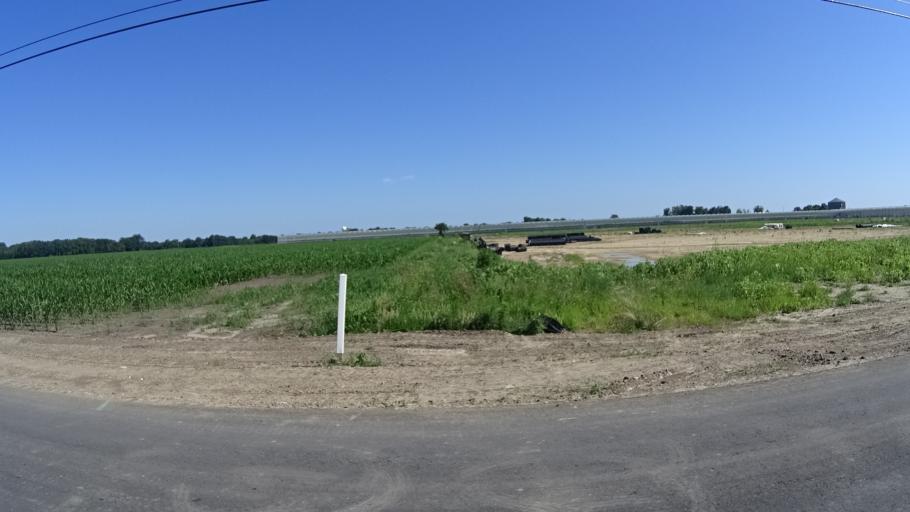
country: US
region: Ohio
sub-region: Erie County
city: Huron
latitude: 41.3892
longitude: -82.5965
